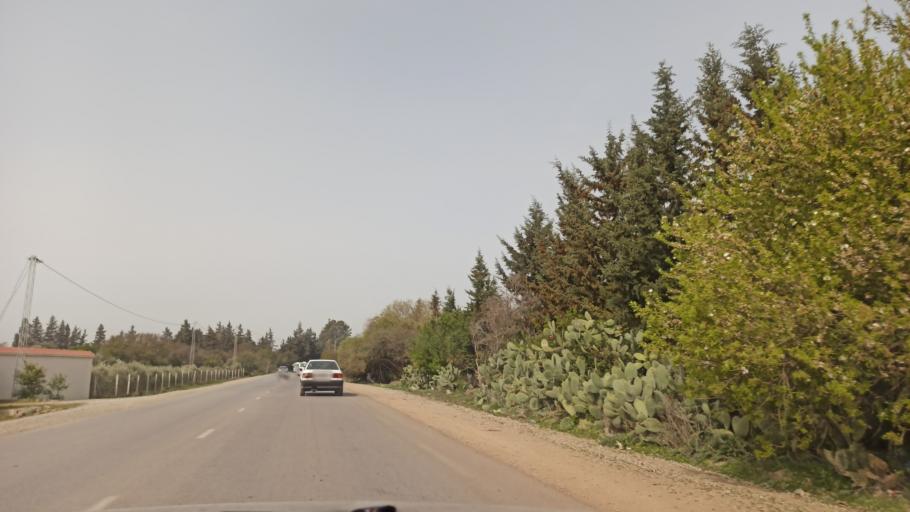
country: TN
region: Zaghwan
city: Zaghouan
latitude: 36.4215
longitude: 10.0978
